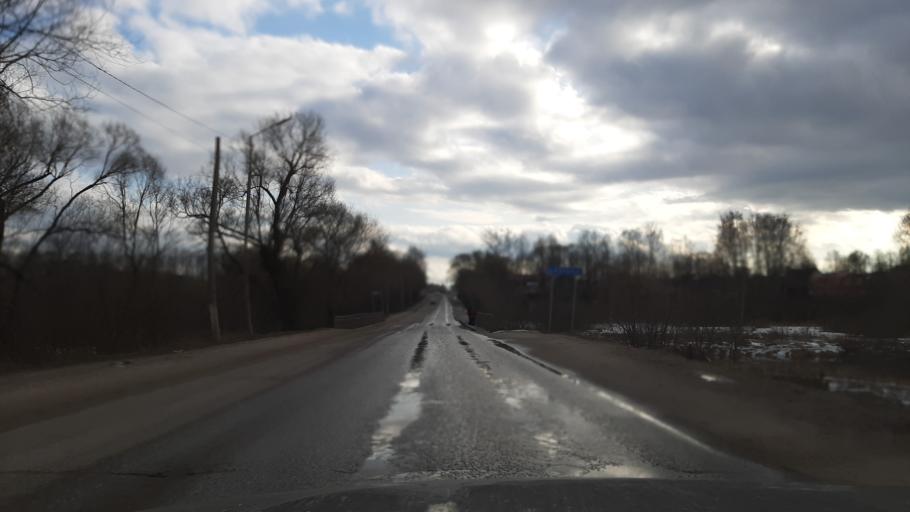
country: RU
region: Ivanovo
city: Teykovo
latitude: 56.8581
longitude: 40.5197
